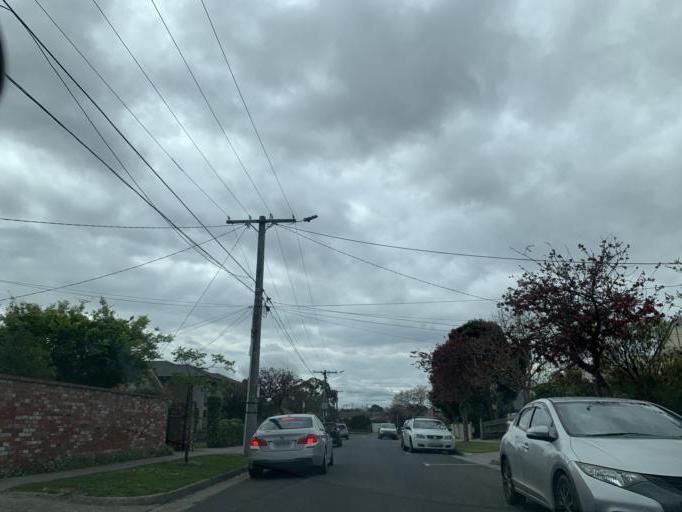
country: AU
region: Victoria
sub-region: Bayside
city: Cheltenham
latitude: -37.9672
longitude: 145.0623
